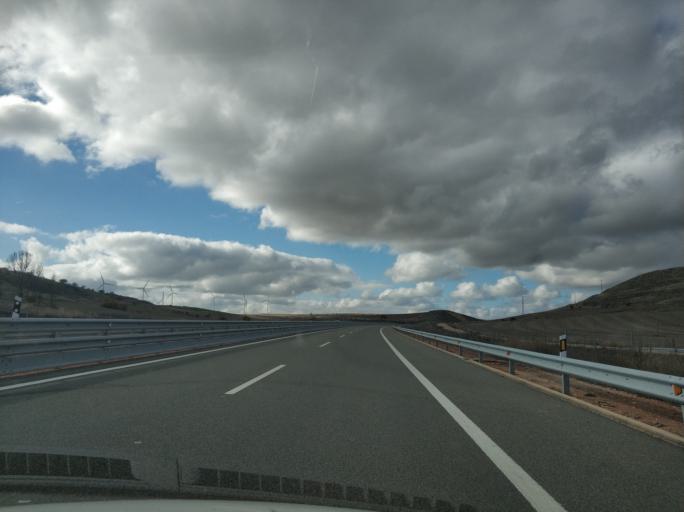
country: ES
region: Castille and Leon
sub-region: Provincia de Soria
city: Medinaceli
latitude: 41.1939
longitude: -2.4482
